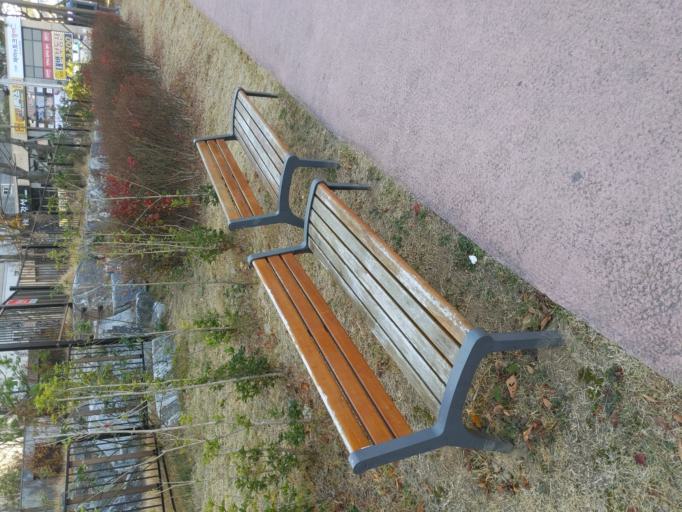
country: KR
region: Daegu
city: Hwawon
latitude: 35.7975
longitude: 128.5293
